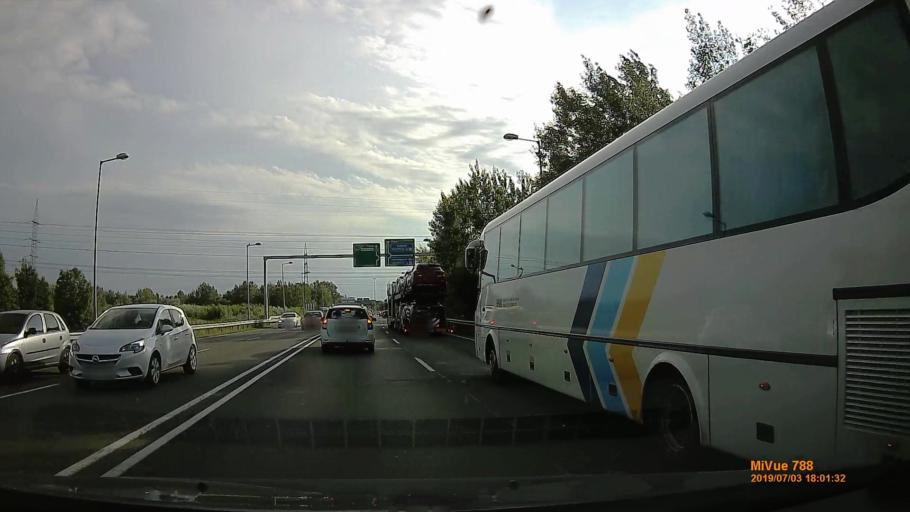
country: HU
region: Gyor-Moson-Sopron
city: Gyor
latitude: 47.6476
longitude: 17.6209
